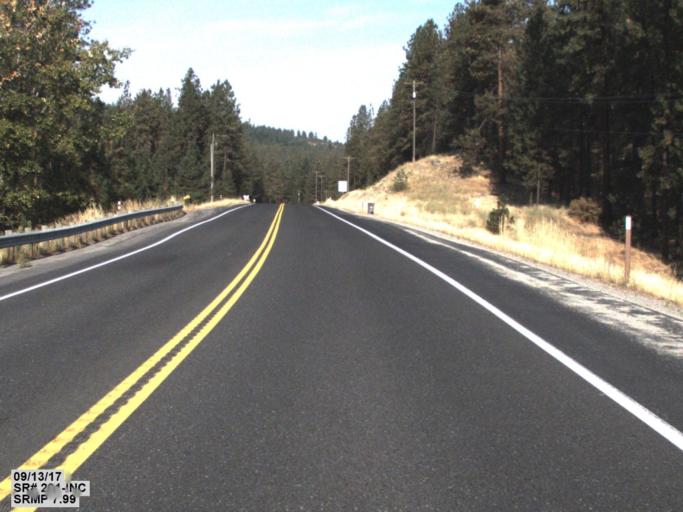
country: US
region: Washington
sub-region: Spokane County
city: Fairwood
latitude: 47.7639
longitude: -117.5407
